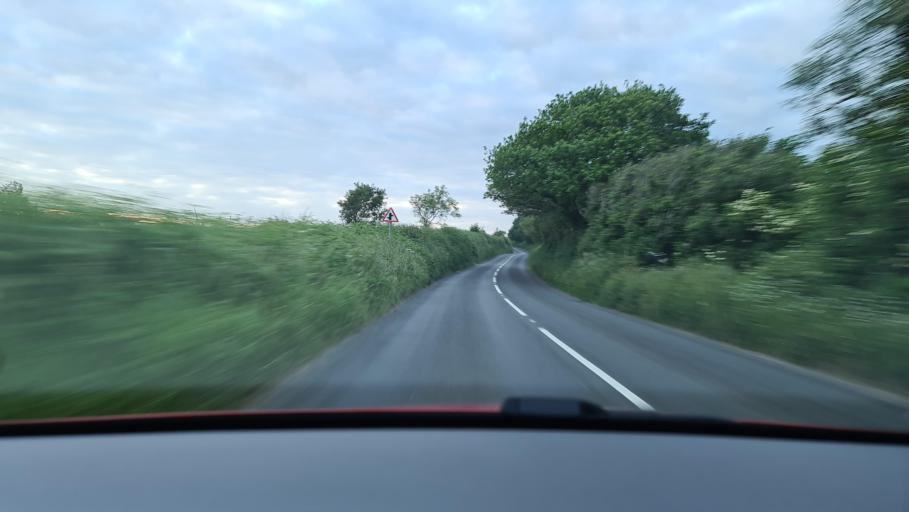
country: GB
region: England
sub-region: Cornwall
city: Liskeard
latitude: 50.4271
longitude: -4.4357
